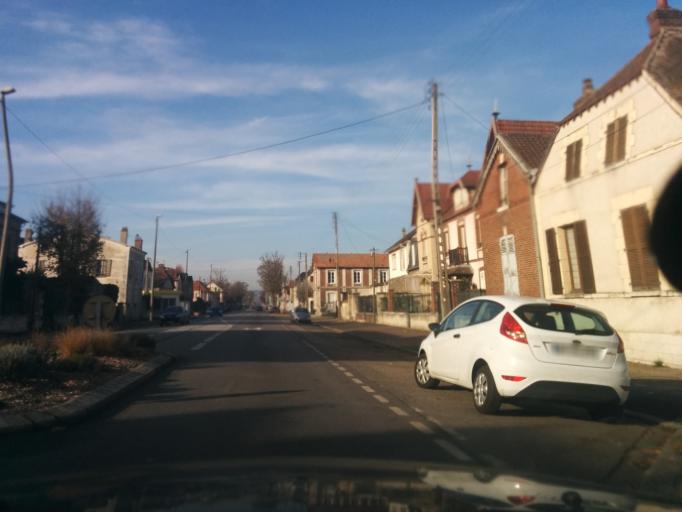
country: FR
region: Haute-Normandie
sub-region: Departement de l'Eure
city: Vernon
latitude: 49.0968
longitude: 1.4810
